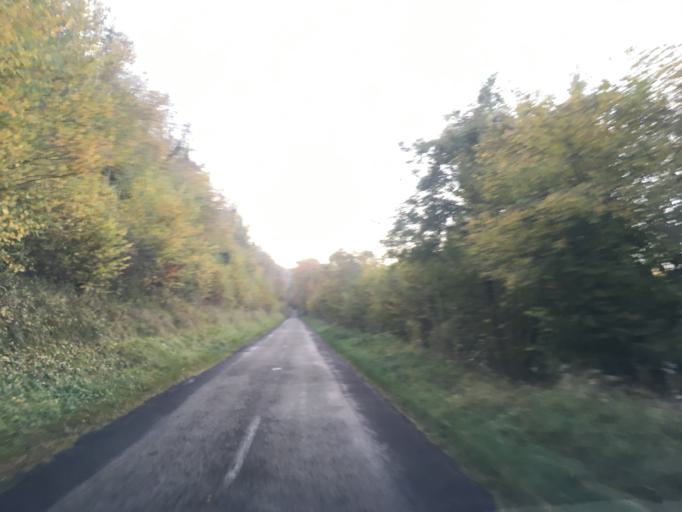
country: FR
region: Haute-Normandie
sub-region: Departement de l'Eure
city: Heudreville-sur-Eure
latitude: 49.1085
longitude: 1.2172
